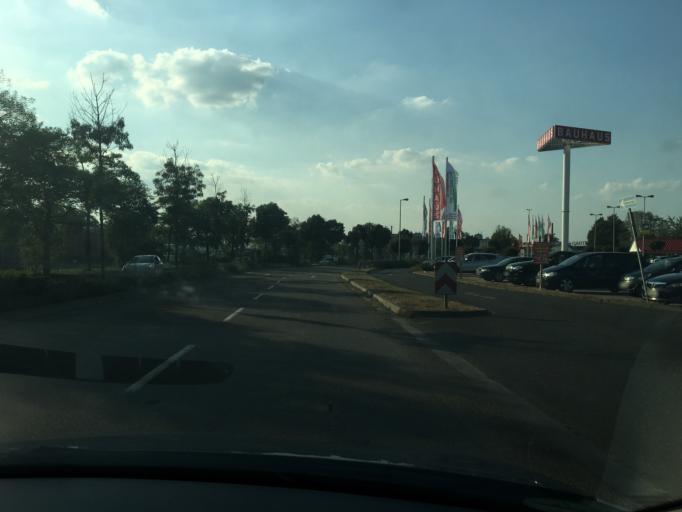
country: DE
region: Hesse
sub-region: Regierungsbezirk Darmstadt
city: Hanau am Main
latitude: 50.1136
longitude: 8.9293
